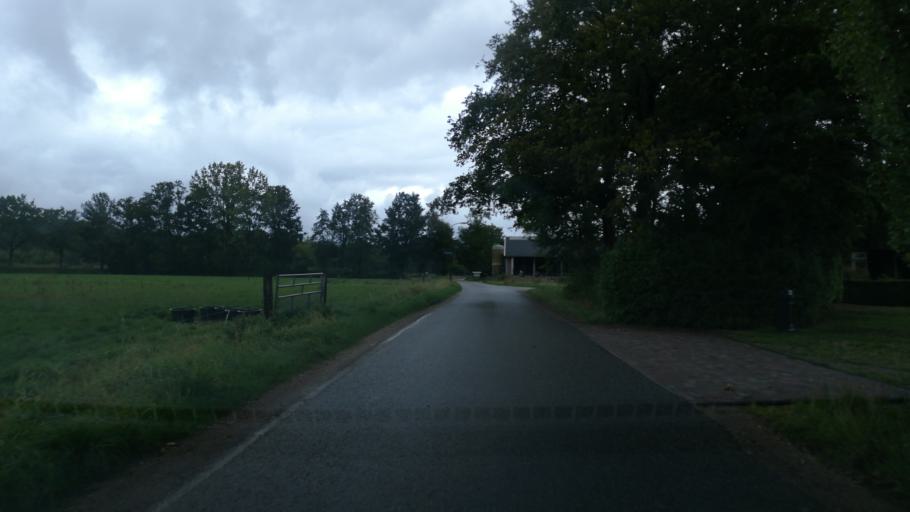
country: NL
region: Gelderland
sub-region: Gemeente Epe
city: Vaassen
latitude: 52.2676
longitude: 5.9891
